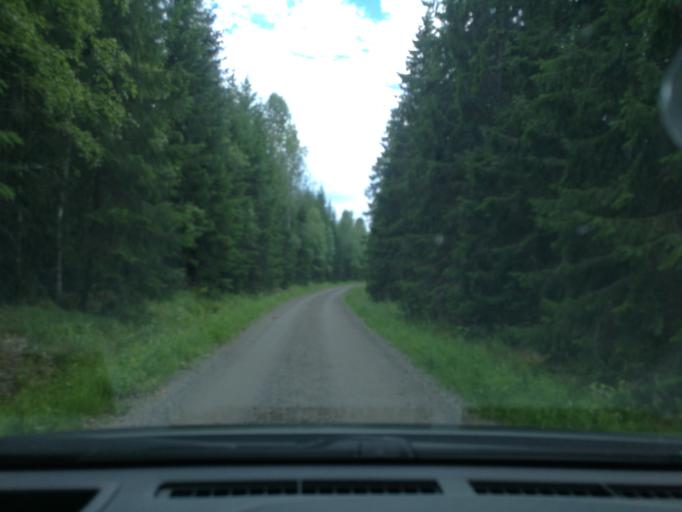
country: SE
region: Vaestmanland
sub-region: Surahammars Kommun
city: Ramnas
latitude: 59.8113
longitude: 16.3076
